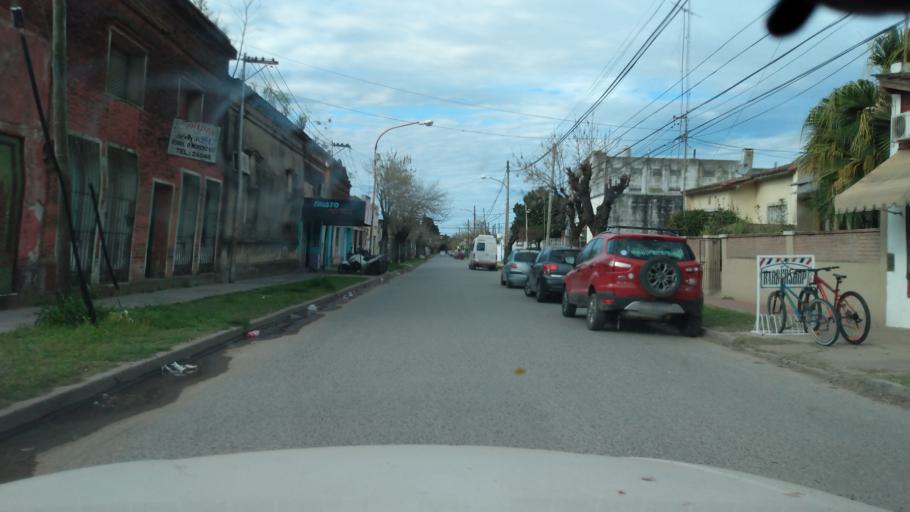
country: AR
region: Buenos Aires
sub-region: Partido de Lujan
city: Lujan
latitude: -34.5682
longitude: -59.1328
